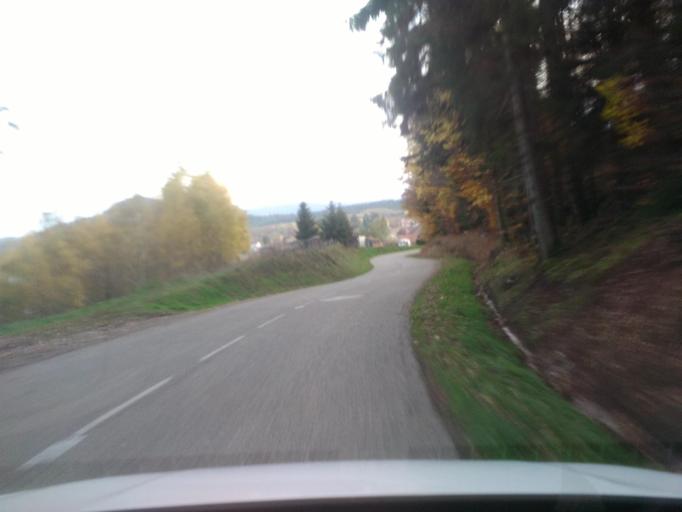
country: FR
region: Lorraine
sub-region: Departement des Vosges
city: Ban-de-Laveline
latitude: 48.3558
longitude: 7.1057
